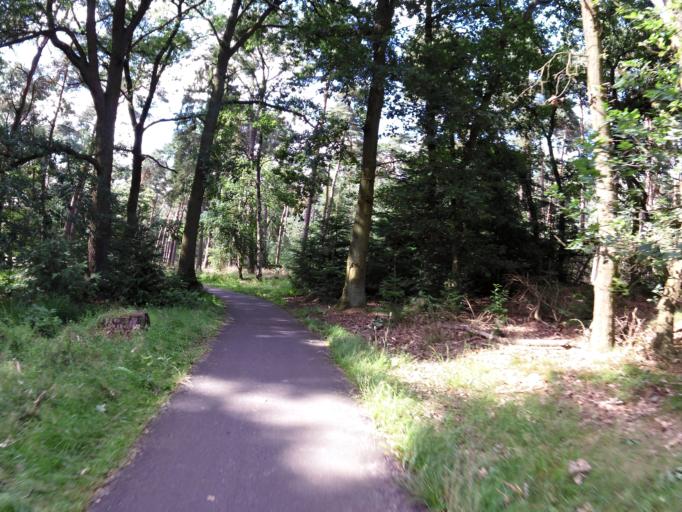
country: NL
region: North Brabant
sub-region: Gemeente Valkenswaard
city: Valkenswaard
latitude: 51.3533
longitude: 5.5146
